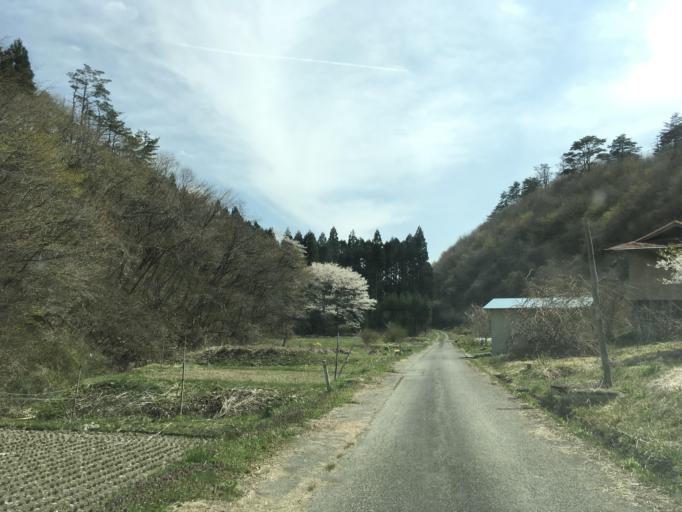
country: JP
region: Iwate
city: Ichinoseki
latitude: 38.8203
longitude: 141.3461
